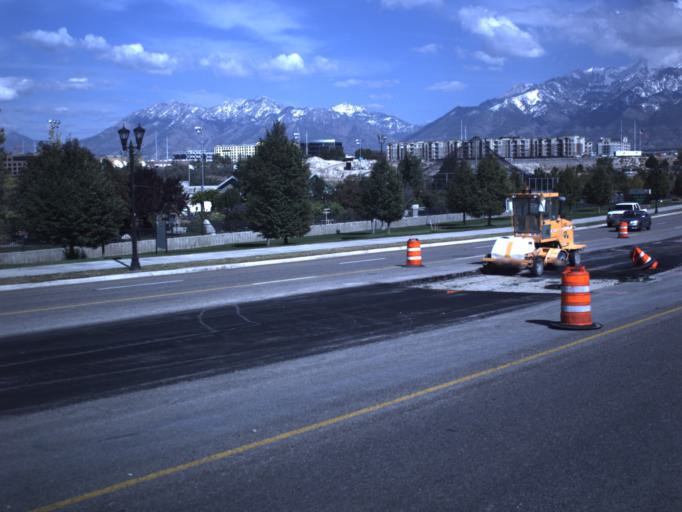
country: US
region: Utah
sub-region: Salt Lake County
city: South Jordan
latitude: 40.5589
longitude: -111.9122
